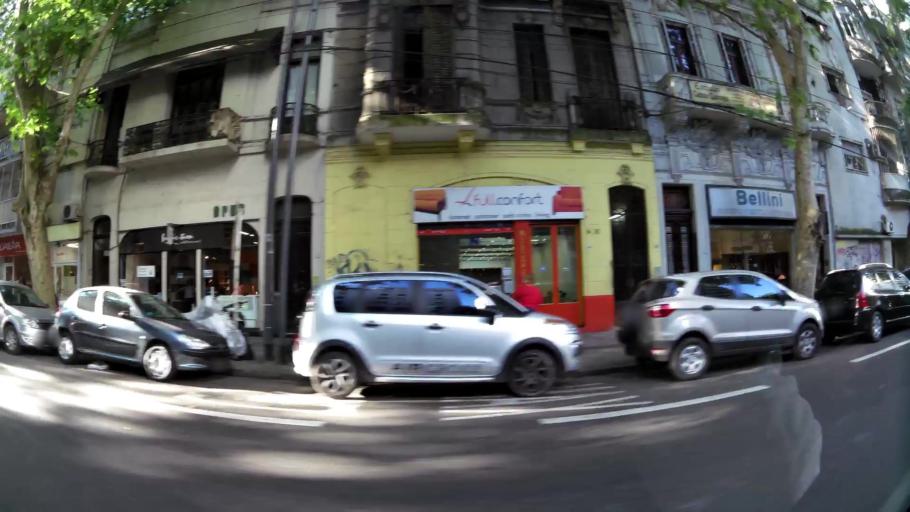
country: AR
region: Buenos Aires F.D.
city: Buenos Aires
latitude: -34.6146
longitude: -58.4035
